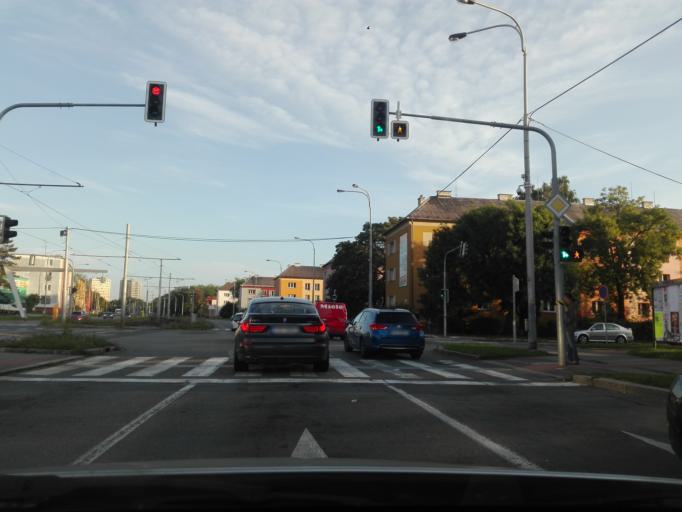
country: CZ
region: Moravskoslezsky
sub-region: Okres Ostrava-Mesto
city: Ostrava
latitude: 49.7882
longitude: 18.2558
